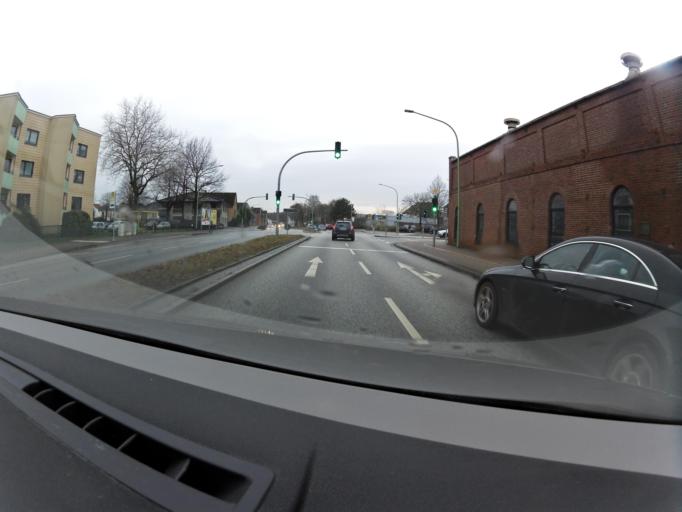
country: DE
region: Bremen
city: Bremerhaven
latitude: 53.5443
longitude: 8.5916
